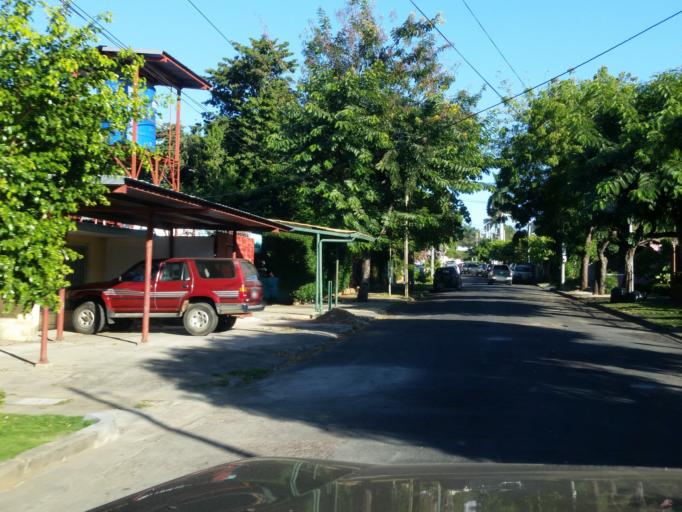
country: NI
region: Managua
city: Managua
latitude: 12.1391
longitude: -86.2785
